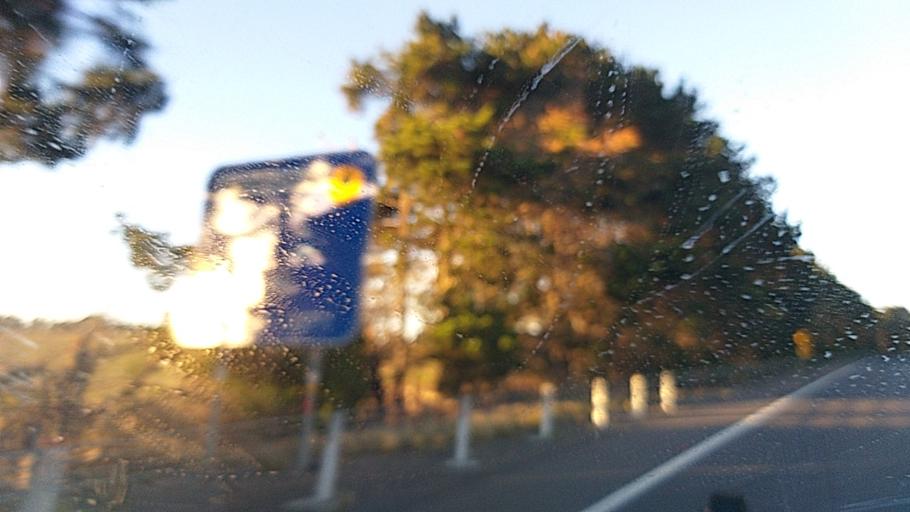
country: AU
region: New South Wales
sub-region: Goulburn Mulwaree
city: Goulburn
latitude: -34.8887
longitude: 149.5290
